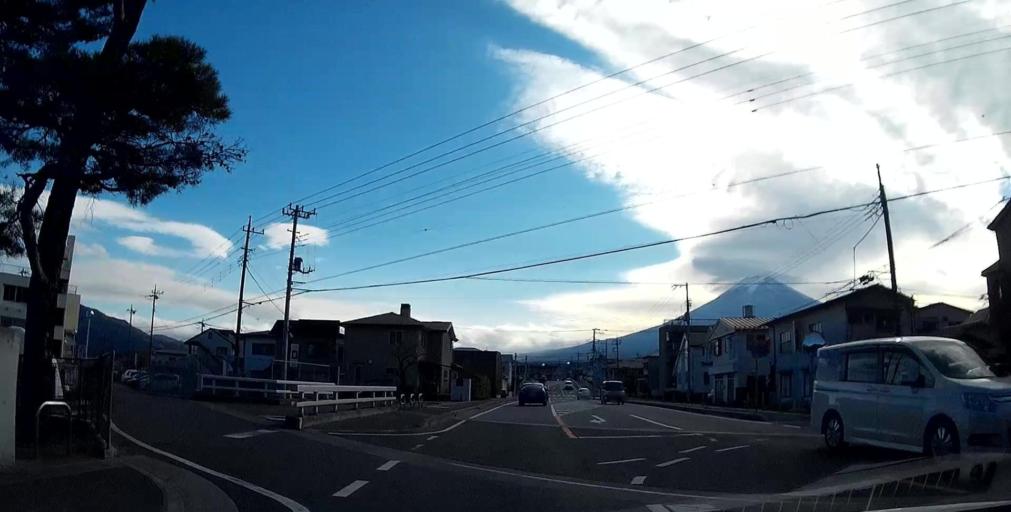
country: JP
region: Yamanashi
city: Fujikawaguchiko
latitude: 35.4930
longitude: 138.7934
